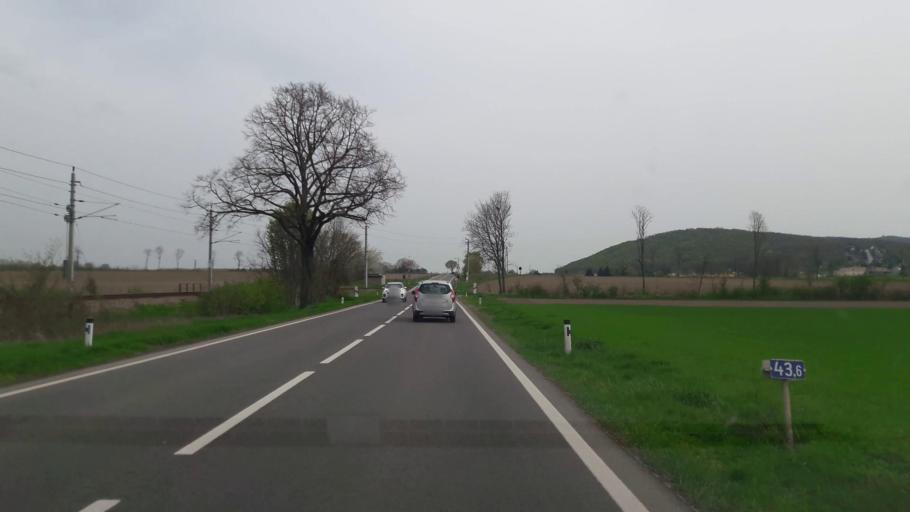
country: AT
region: Lower Austria
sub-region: Politischer Bezirk Bruck an der Leitha
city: Wolfsthal
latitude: 48.1402
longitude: 16.9924
